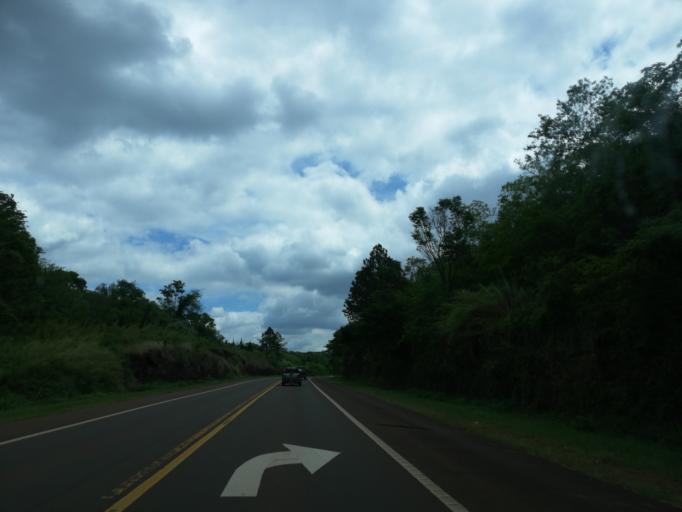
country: AR
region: Misiones
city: Arroyo del Medio
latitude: -27.6437
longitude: -55.4007
